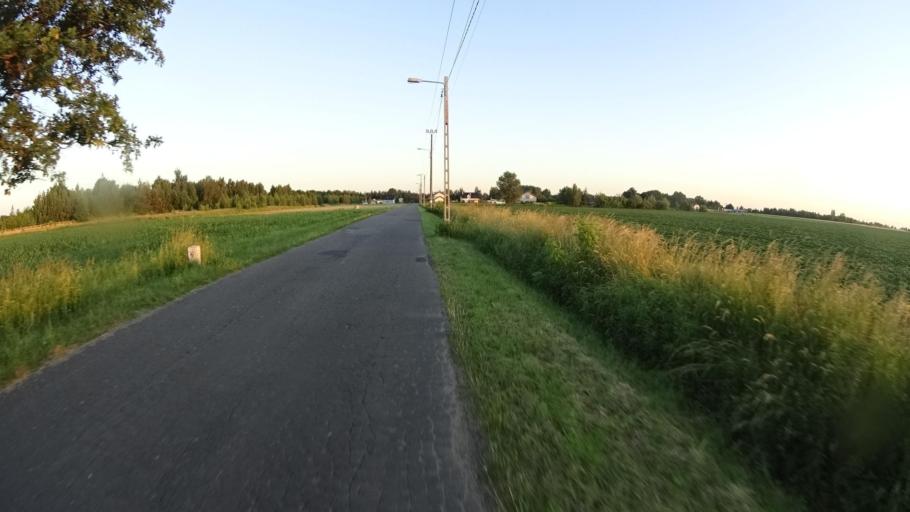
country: PL
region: Masovian Voivodeship
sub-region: Powiat warszawski zachodni
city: Jozefow
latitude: 52.2517
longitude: 20.6741
